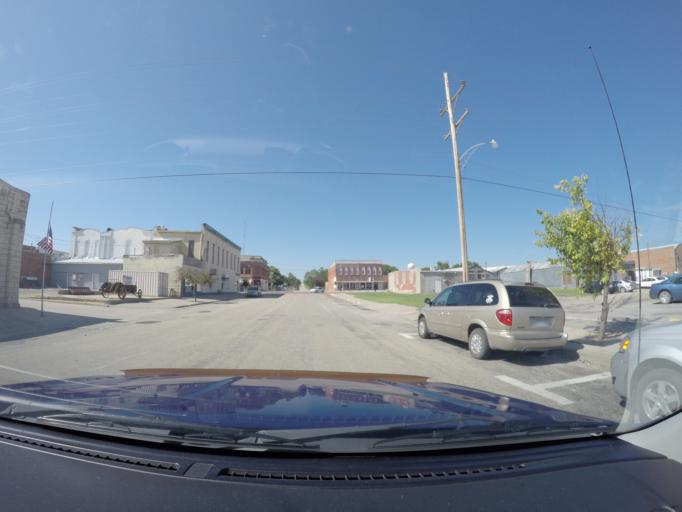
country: US
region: Kansas
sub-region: Rooks County
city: Stockton
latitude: 39.4360
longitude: -99.2737
